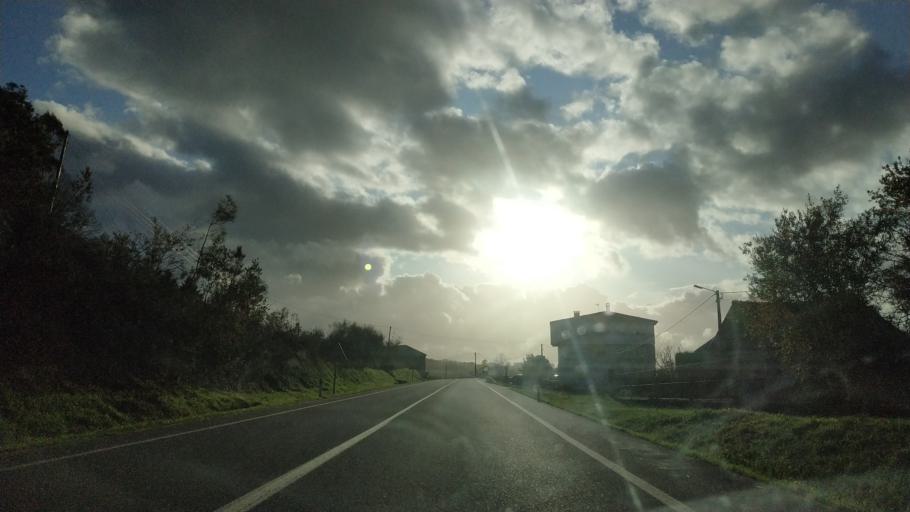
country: ES
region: Galicia
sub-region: Provincia de Pontevedra
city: Silleda
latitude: 42.7853
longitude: -8.1690
